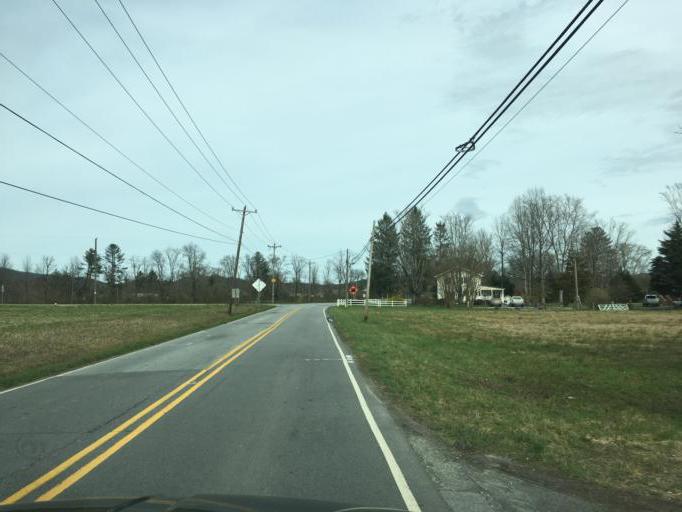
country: US
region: North Carolina
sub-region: Transylvania County
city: Brevard
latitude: 35.2485
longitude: -82.7098
